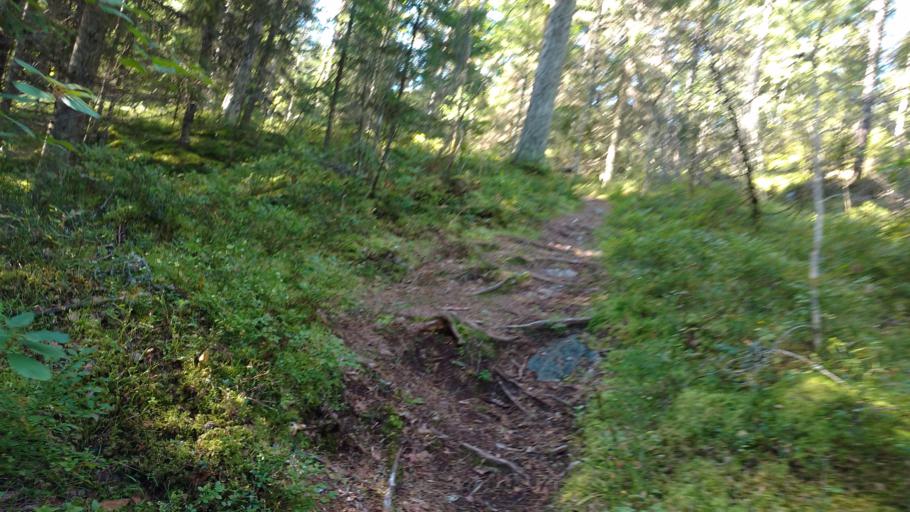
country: FI
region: Varsinais-Suomi
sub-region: Salo
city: Salo
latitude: 60.3828
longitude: 23.1693
